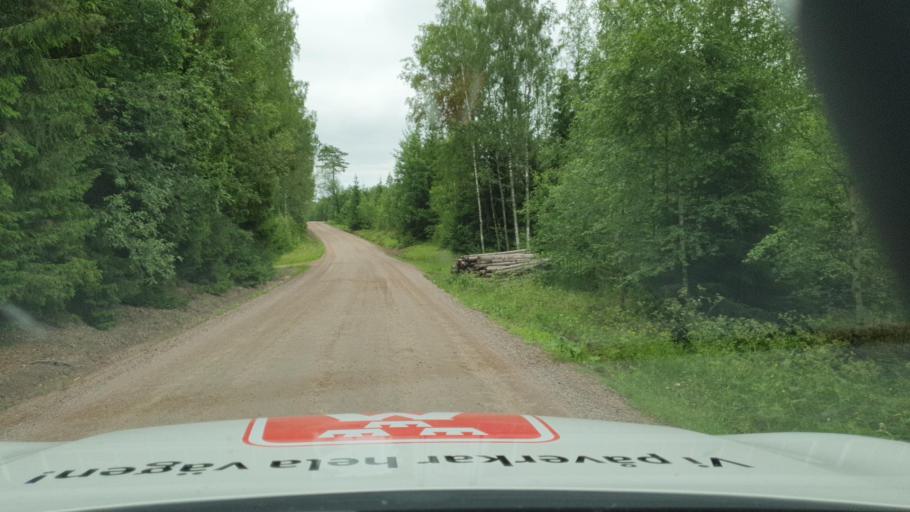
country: SE
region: Vaermland
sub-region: Kristinehamns Kommun
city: Kristinehamn
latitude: 59.5259
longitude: 13.9621
